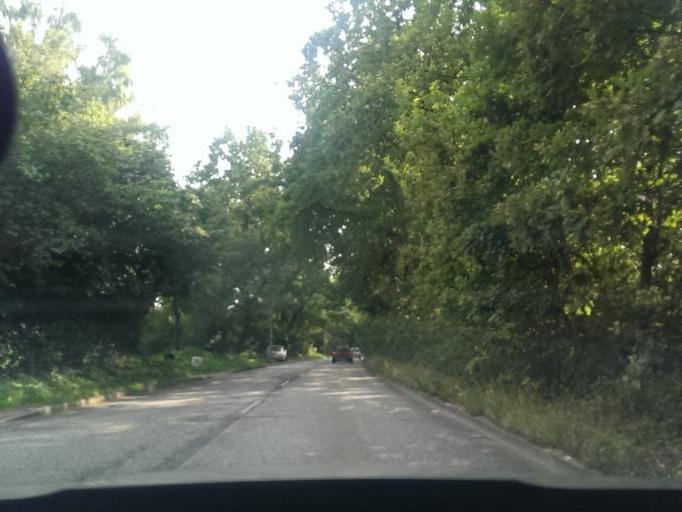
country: DE
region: Hamburg
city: Lemsahl-Mellingstedt
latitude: 53.6779
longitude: 10.0942
